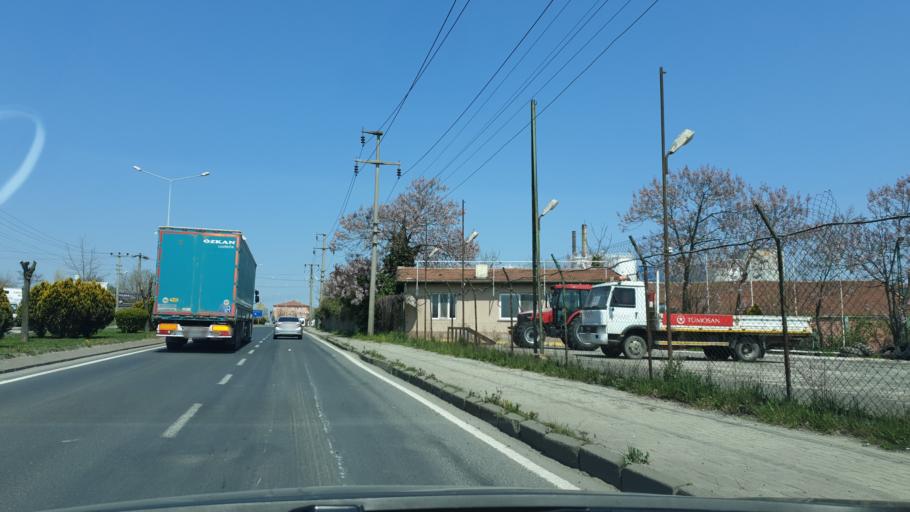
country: TR
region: Tekirdag
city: Corlu
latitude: 41.1606
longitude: 27.7864
